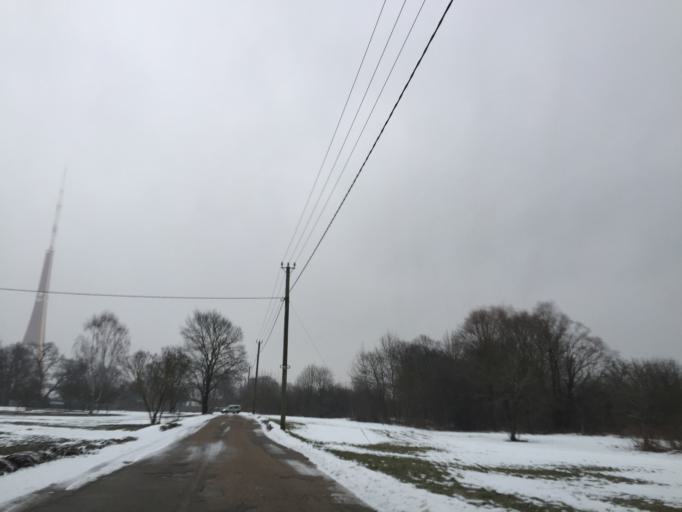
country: LV
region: Riga
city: Riga
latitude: 56.9255
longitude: 24.1216
